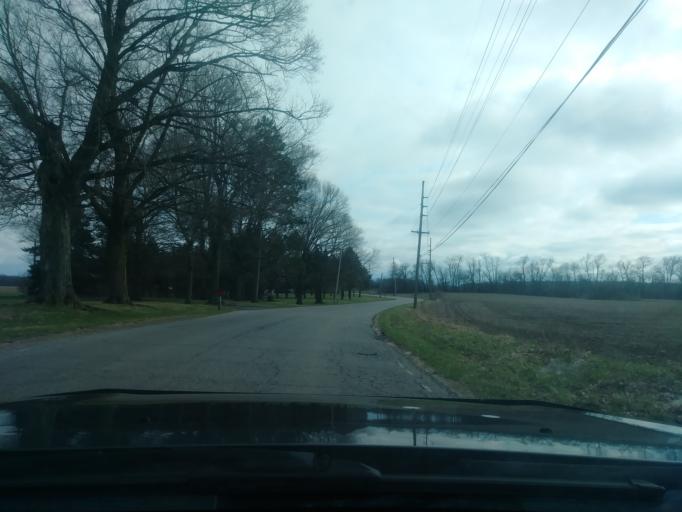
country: US
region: Indiana
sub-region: LaPorte County
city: LaPorte
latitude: 41.6075
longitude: -86.7973
